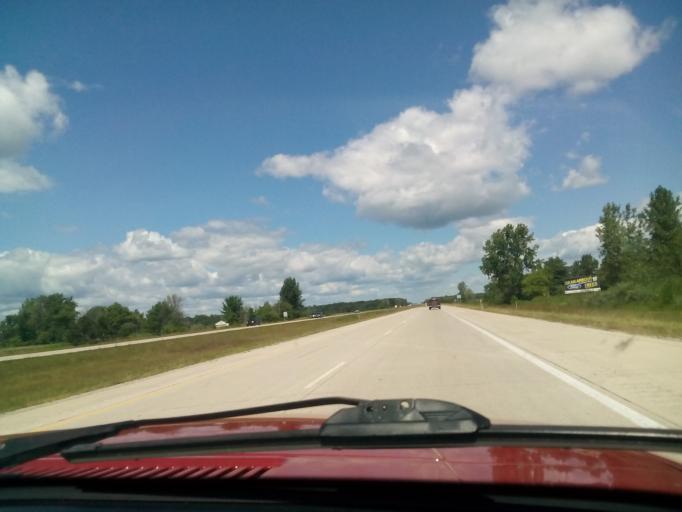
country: US
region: Michigan
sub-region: Bay County
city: Pinconning
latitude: 43.8087
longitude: -84.0205
